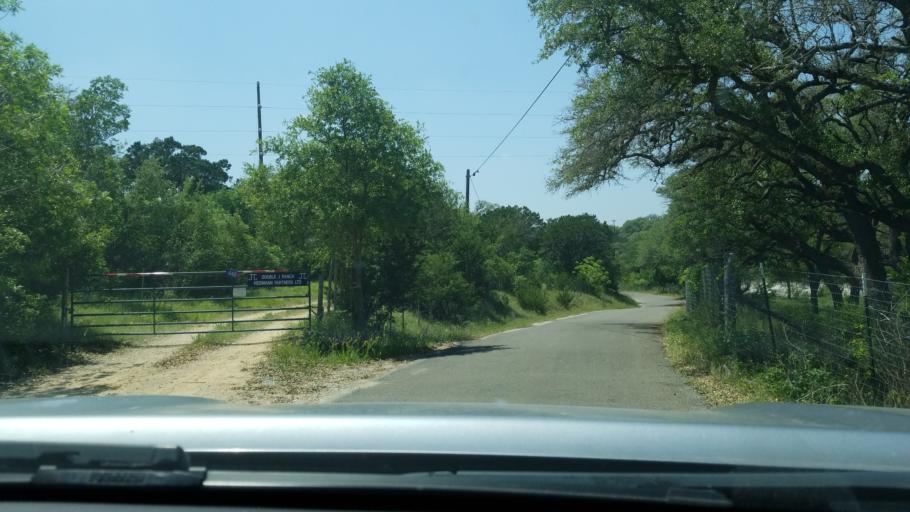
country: US
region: Texas
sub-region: Blanco County
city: Blanco
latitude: 30.0011
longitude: -98.4112
